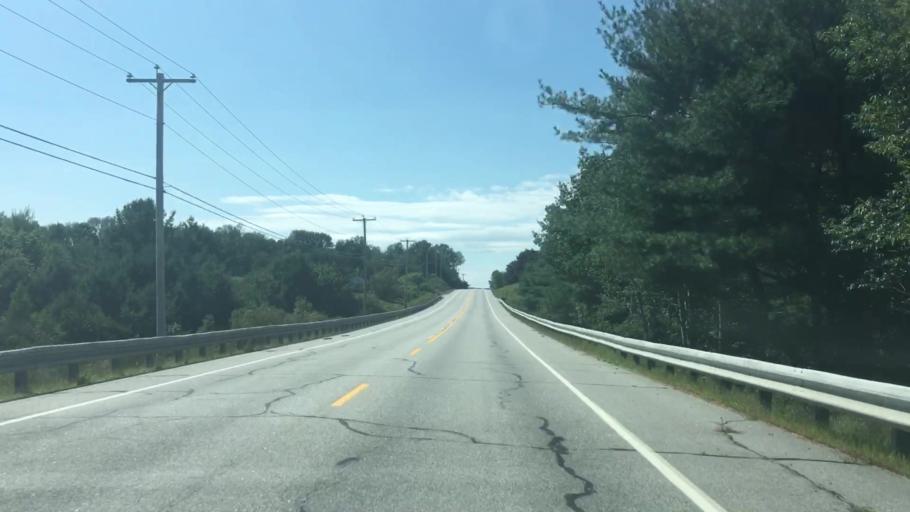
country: US
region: Maine
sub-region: Kennebec County
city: Monmouth
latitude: 44.1691
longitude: -70.0151
